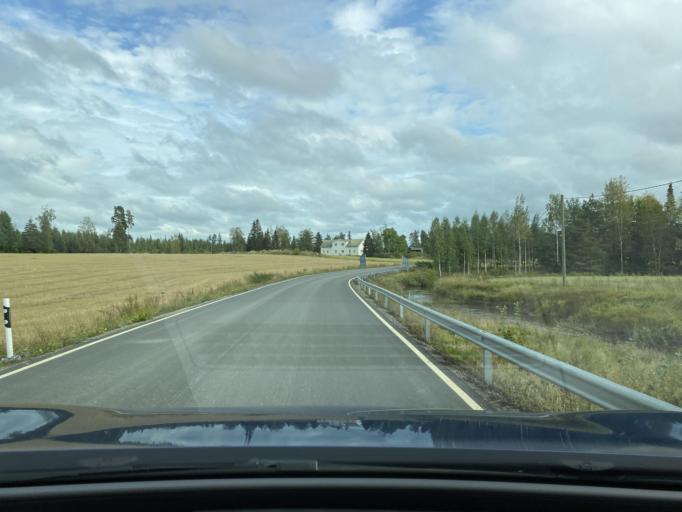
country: FI
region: Pirkanmaa
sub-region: Lounais-Pirkanmaa
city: Punkalaidun
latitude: 61.2320
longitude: 23.1369
